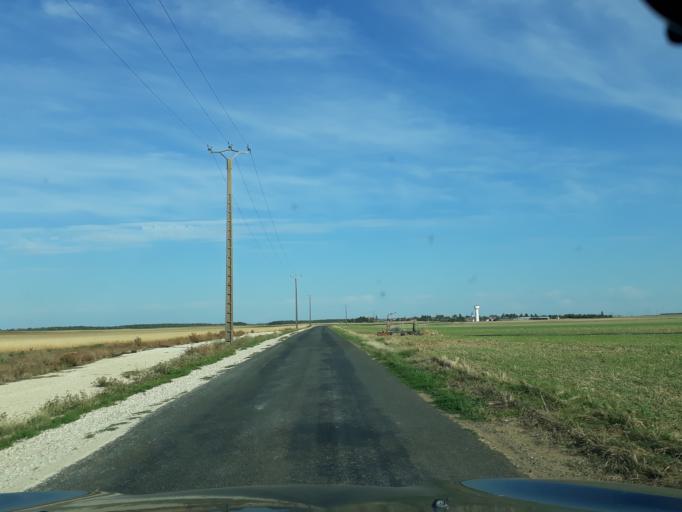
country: FR
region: Centre
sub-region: Departement du Loir-et-Cher
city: Ouzouer-le-Marche
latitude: 47.9356
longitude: 1.5549
